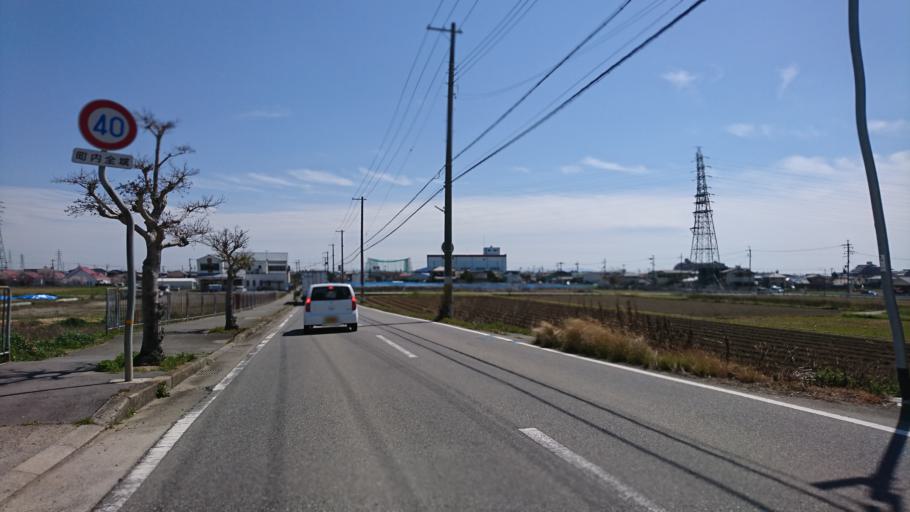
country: JP
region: Hyogo
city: Kakogawacho-honmachi
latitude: 34.7336
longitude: 134.8991
